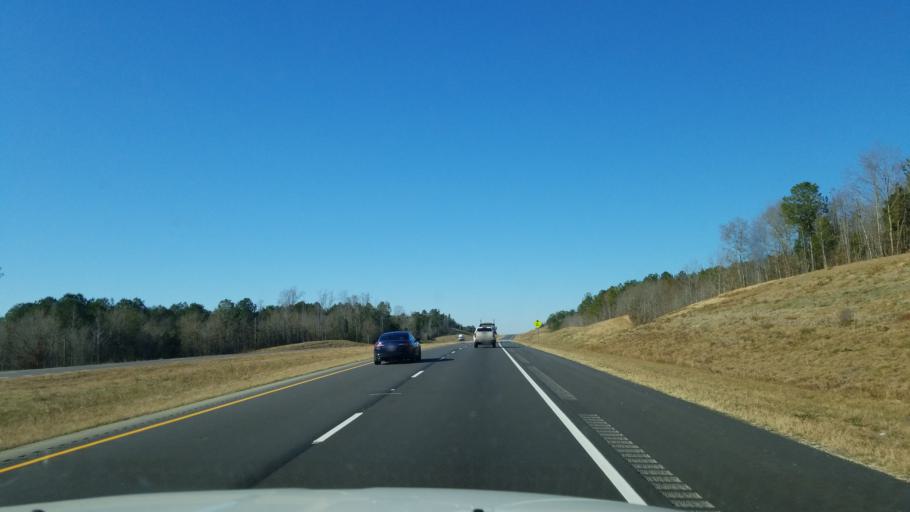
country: US
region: Alabama
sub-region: Pickens County
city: Reform
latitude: 33.3530
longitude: -87.9617
